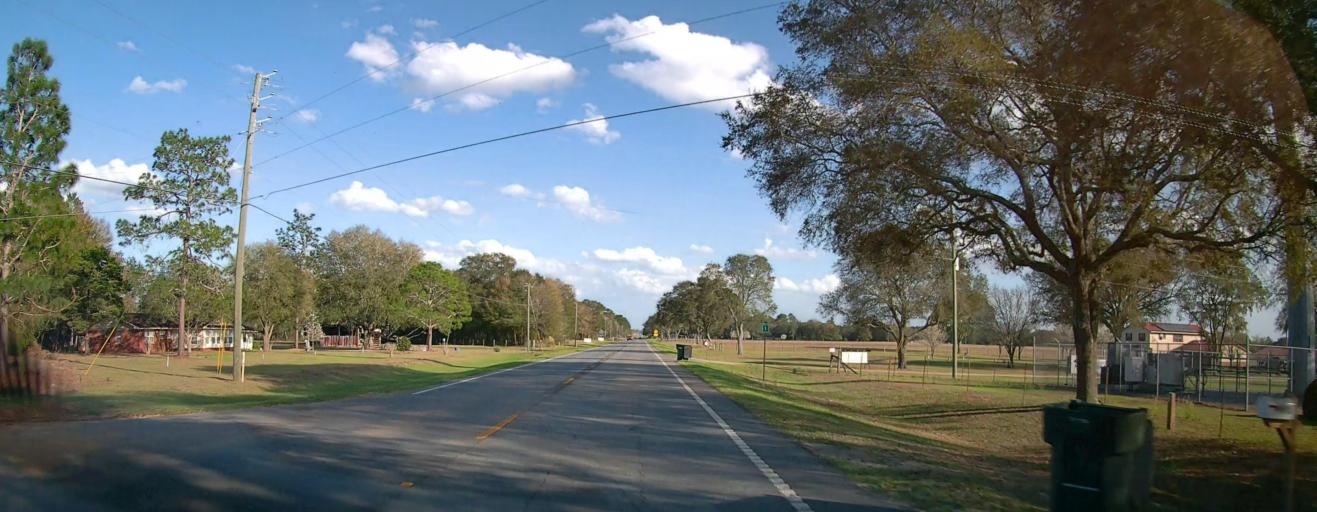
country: US
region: Georgia
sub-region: Tattnall County
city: Reidsville
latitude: 32.1128
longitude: -82.1815
